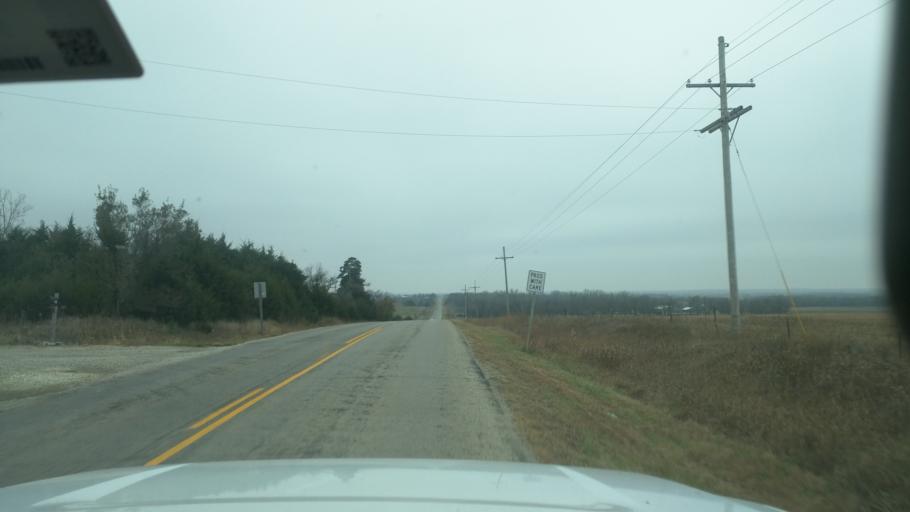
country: US
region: Kansas
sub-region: Lyon County
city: Emporia
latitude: 38.5670
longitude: -96.2611
